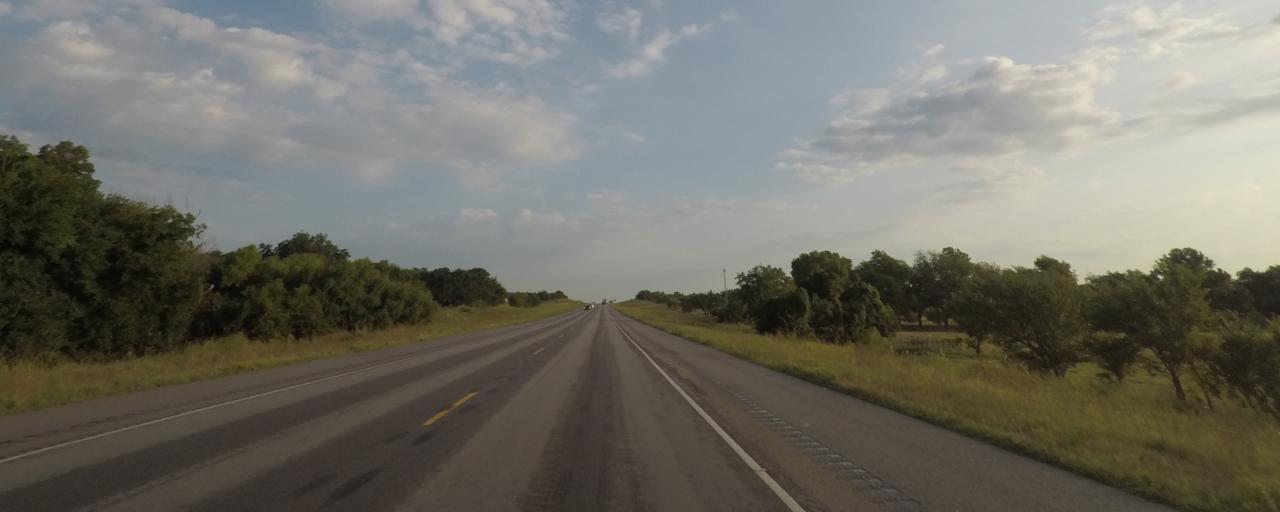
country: US
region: Oklahoma
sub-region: Stephens County
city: Meridian
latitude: 34.4432
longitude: -97.9741
